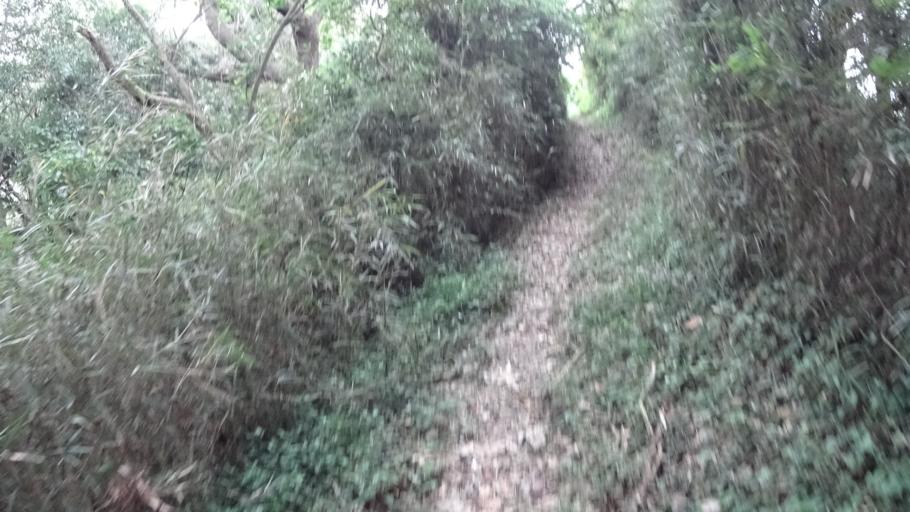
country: JP
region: Kanagawa
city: Zushi
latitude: 35.2993
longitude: 139.6197
